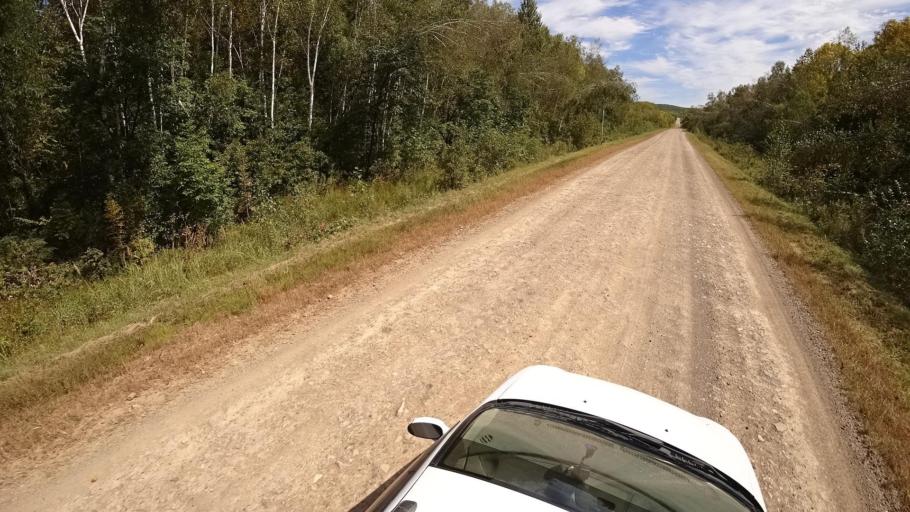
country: RU
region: Primorskiy
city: Yakovlevka
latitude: 44.6599
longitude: 133.7296
